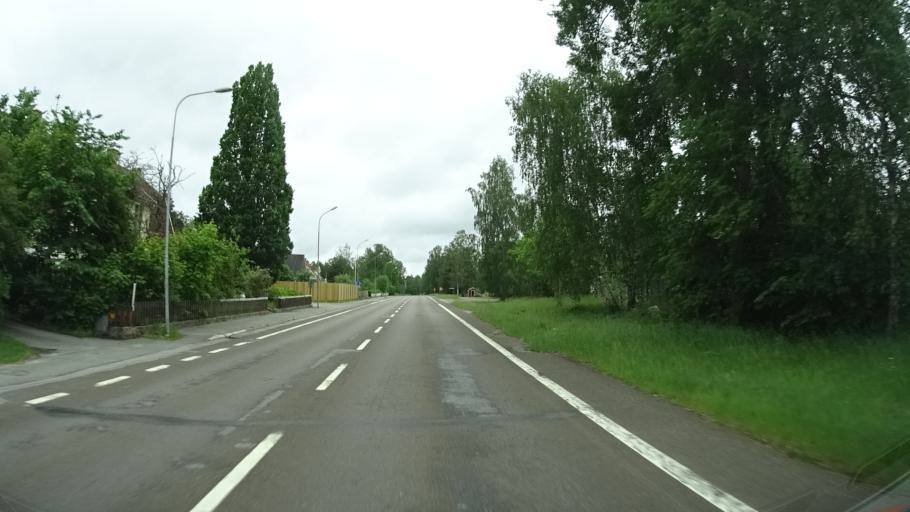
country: SE
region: Kalmar
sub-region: Hultsfreds Kommun
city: Hultsfred
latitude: 57.5524
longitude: 15.7202
